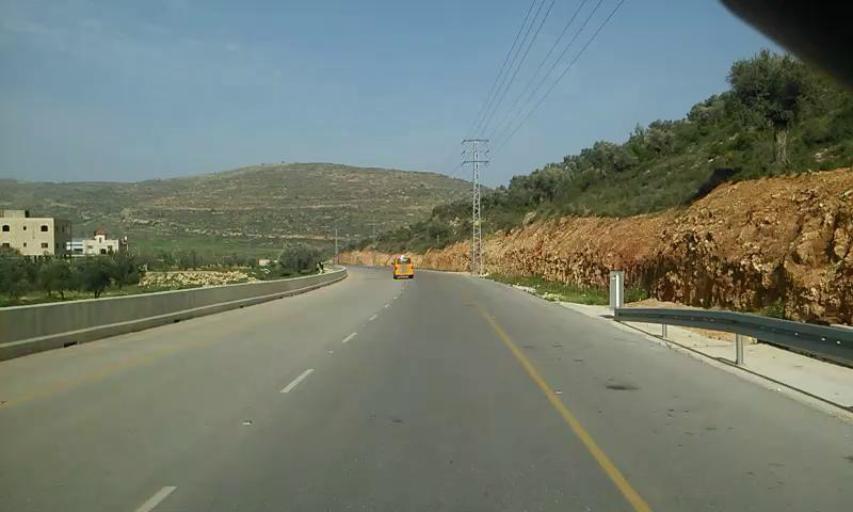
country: PS
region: West Bank
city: Dura al Qar`
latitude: 31.9850
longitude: 35.2310
